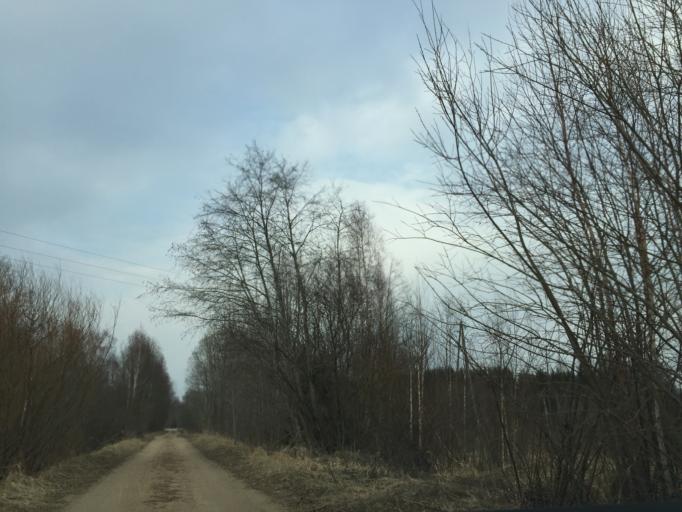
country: LV
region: Priekuli
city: Priekuli
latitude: 57.2112
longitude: 25.4085
